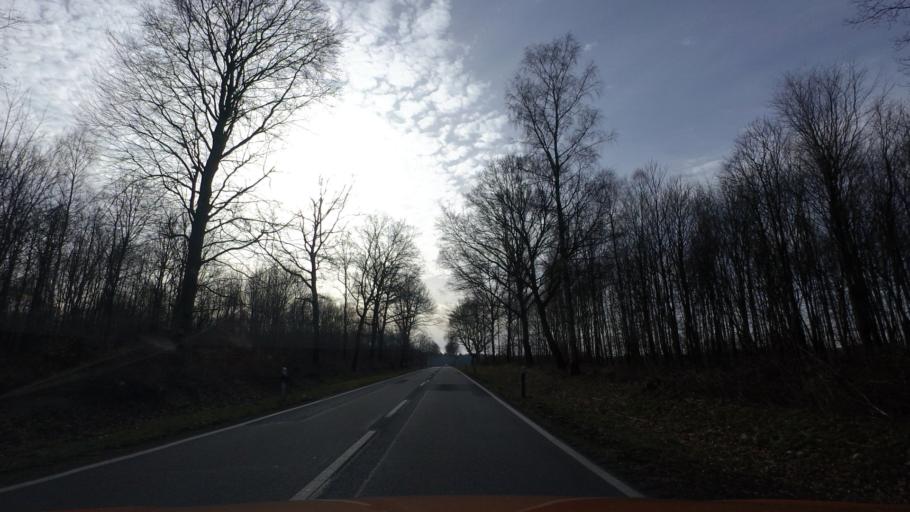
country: DE
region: Lower Saxony
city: Harpstedt
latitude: 52.9073
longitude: 8.6050
